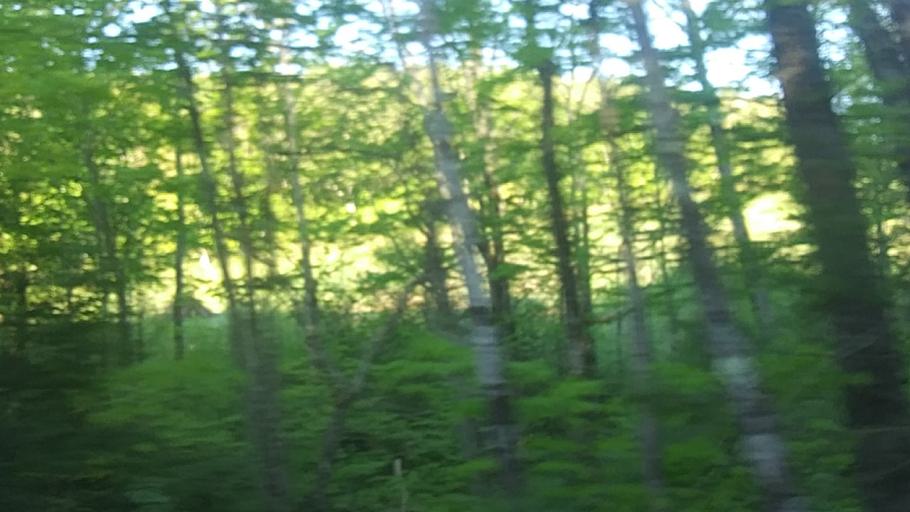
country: US
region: Massachusetts
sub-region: Franklin County
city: Buckland
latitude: 42.5835
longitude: -72.7734
